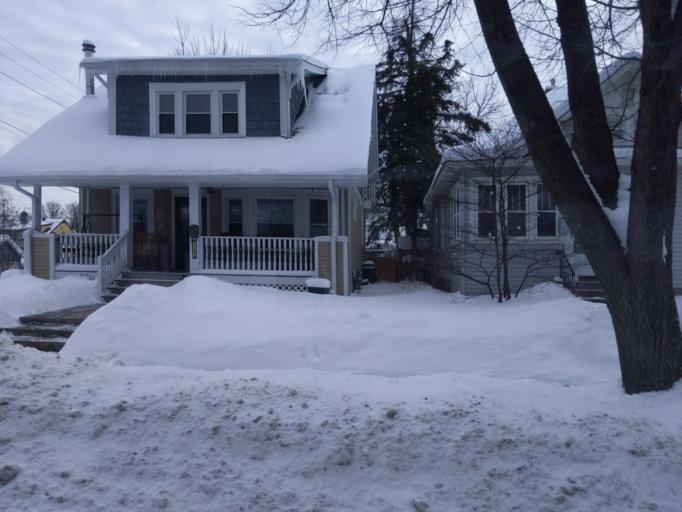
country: US
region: Minnesota
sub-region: Ramsey County
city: Falcon Heights
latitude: 44.9630
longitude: -93.1546
